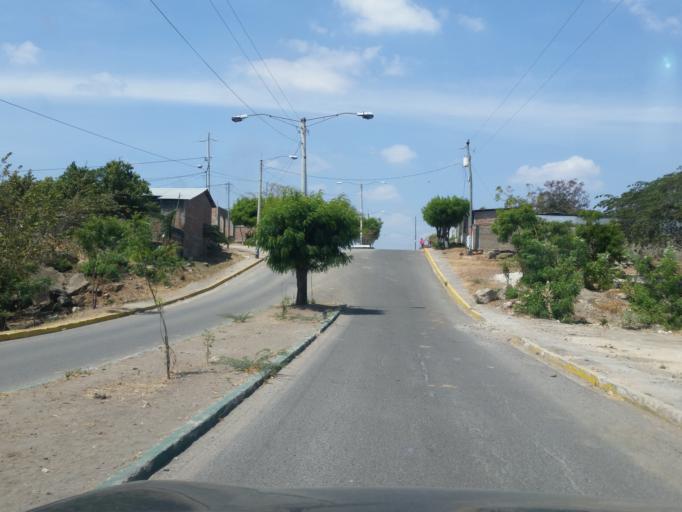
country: NI
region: Matagalpa
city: Ciudad Dario
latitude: 12.7301
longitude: -86.1166
